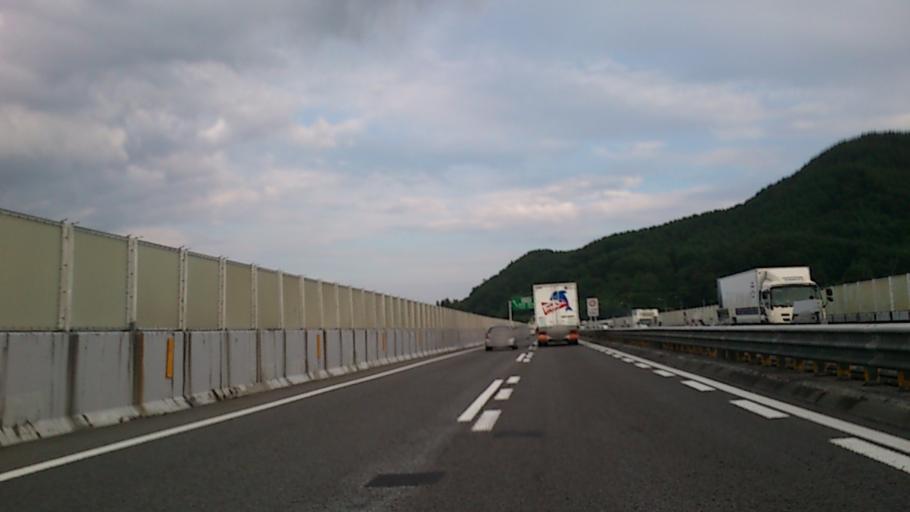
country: JP
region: Nagano
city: Okaya
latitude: 36.0568
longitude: 138.0402
